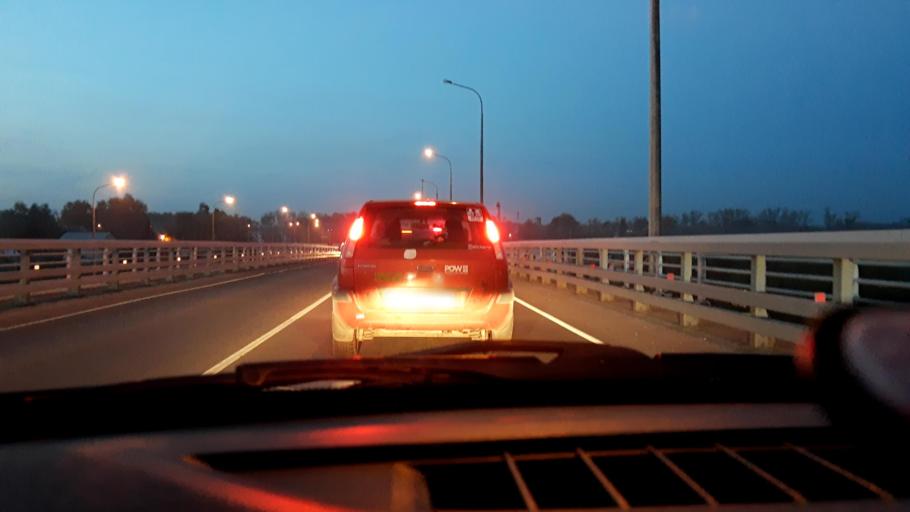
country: RU
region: Nizjnij Novgorod
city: Neklyudovo
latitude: 56.3976
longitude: 43.9902
